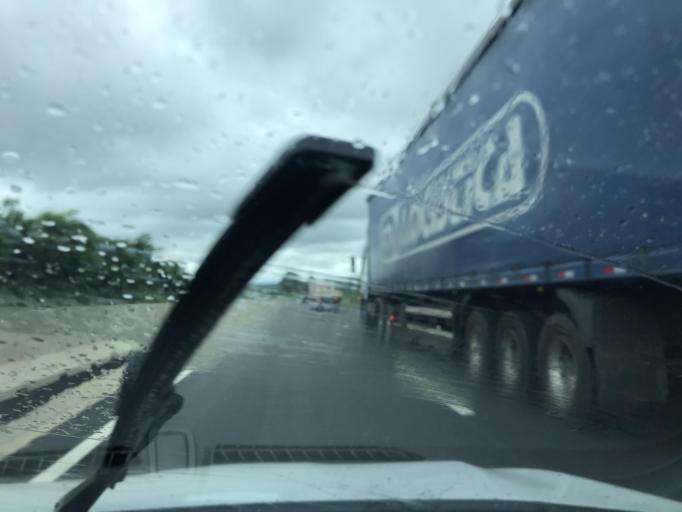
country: BR
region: Goias
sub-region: Catalao
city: Catalao
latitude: -18.2639
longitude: -47.9996
